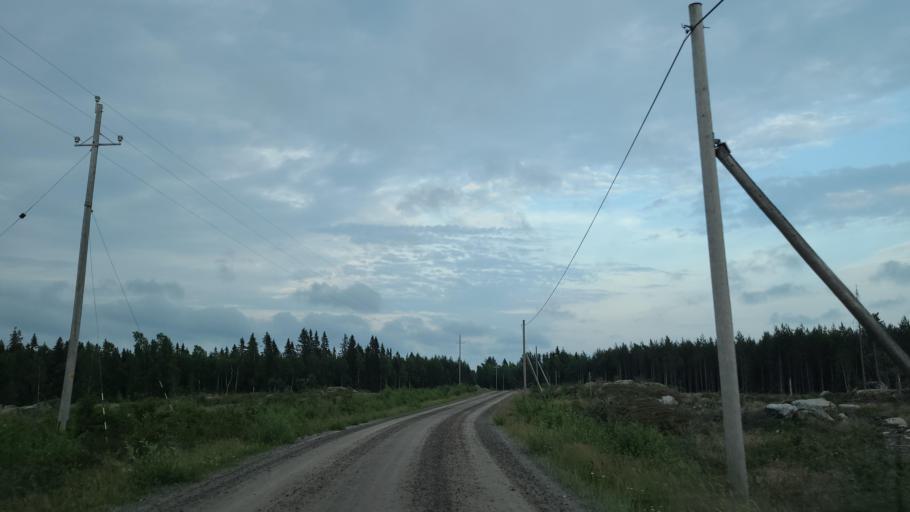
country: FI
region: Ostrobothnia
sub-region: Vaasa
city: Replot
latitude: 63.3180
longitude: 21.1517
